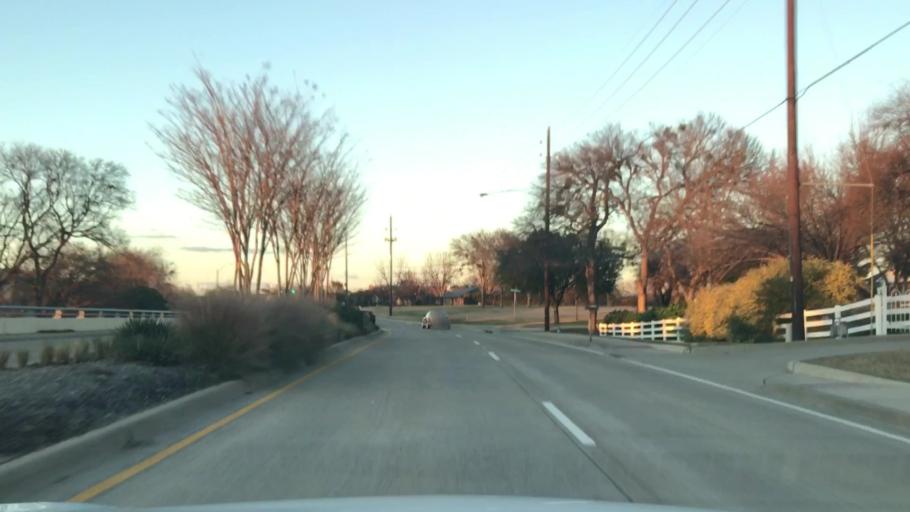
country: US
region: Texas
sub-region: Rockwall County
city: Heath
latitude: 32.8813
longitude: -96.4729
